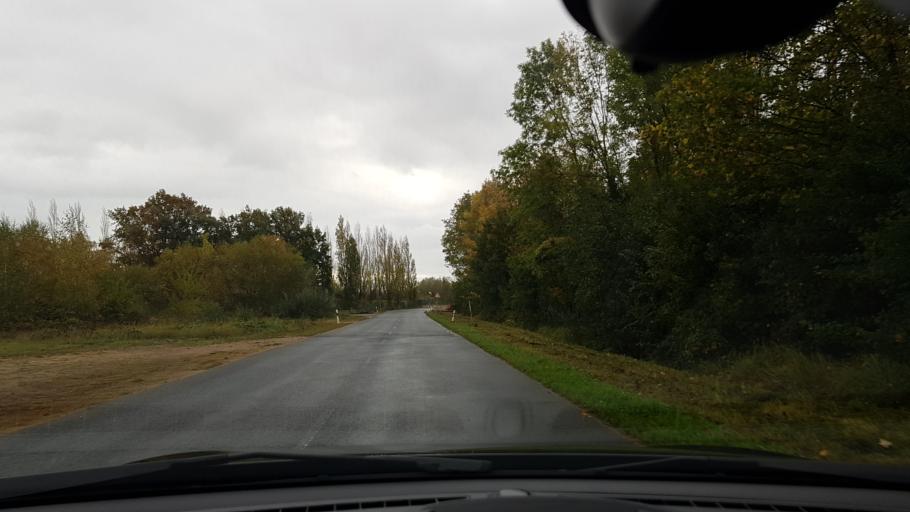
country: DE
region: North Rhine-Westphalia
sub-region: Regierungsbezirk Koln
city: Elsdorf
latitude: 50.9279
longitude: 6.5575
